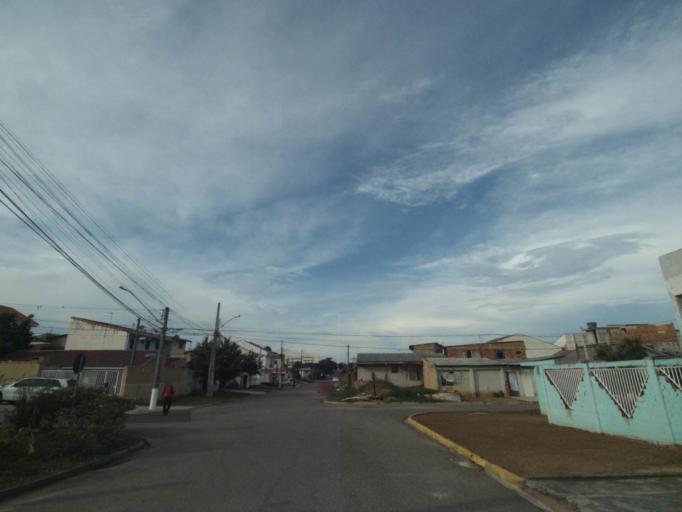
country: BR
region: Parana
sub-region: Pinhais
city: Pinhais
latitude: -25.4497
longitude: -49.2240
